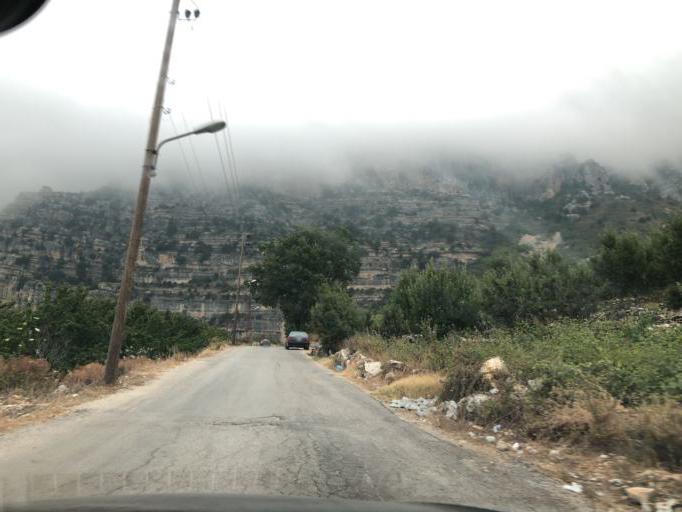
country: LB
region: Liban-Nord
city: Bcharre
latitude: 34.1061
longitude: 35.9049
